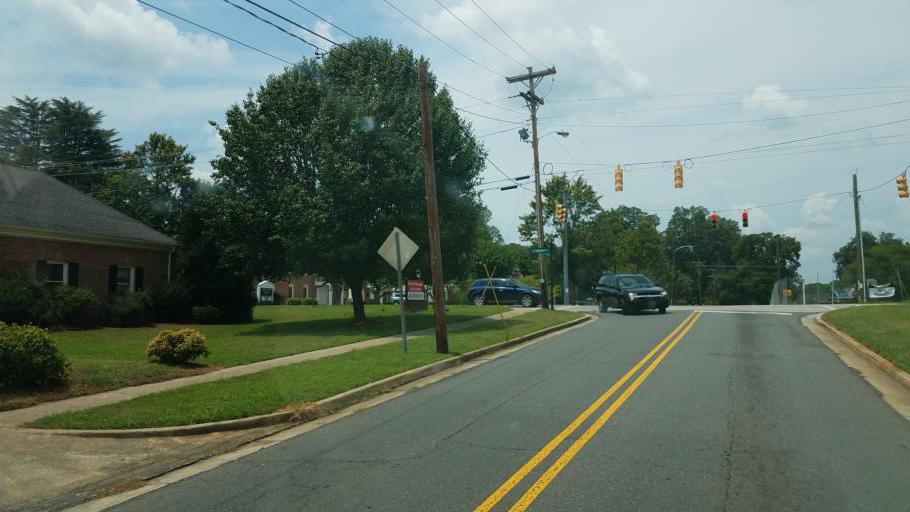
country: US
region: South Carolina
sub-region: York County
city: York
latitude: 34.9920
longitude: -81.2430
